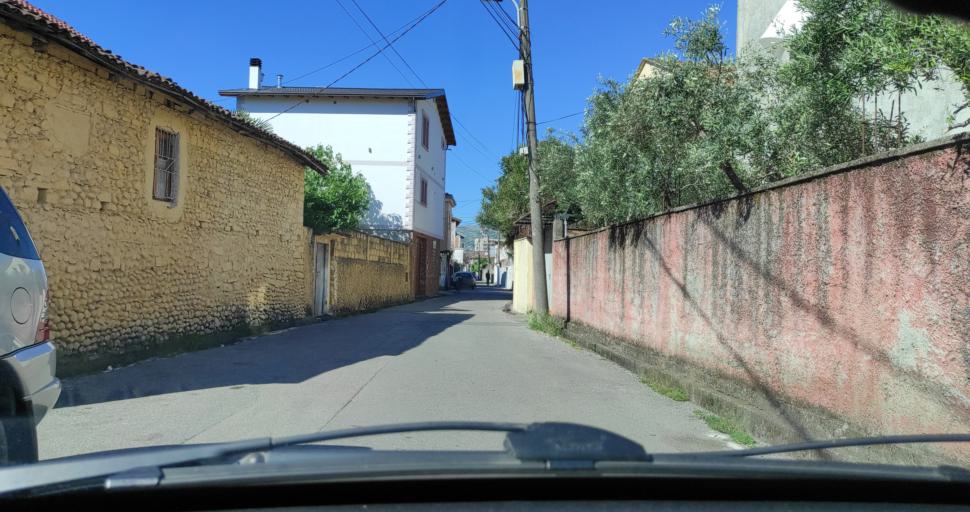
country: AL
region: Shkoder
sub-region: Rrethi i Shkodres
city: Shkoder
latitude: 42.0704
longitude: 19.5208
